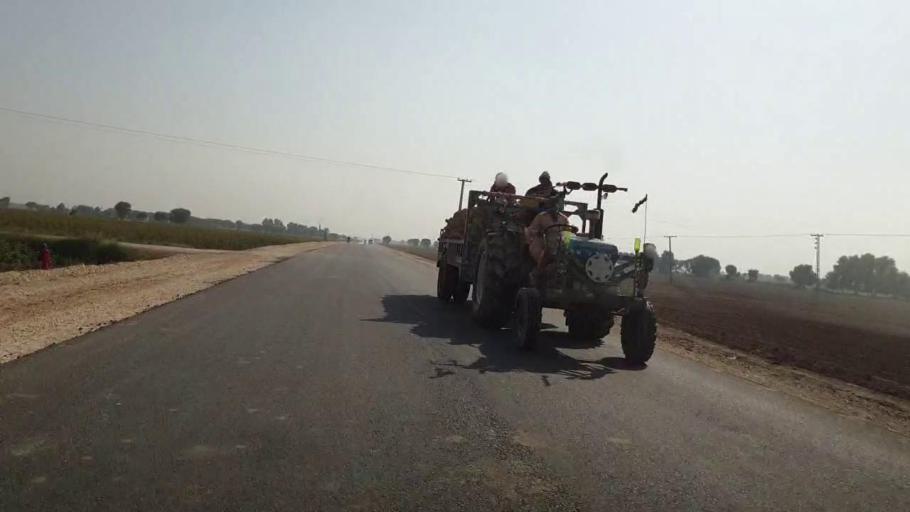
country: PK
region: Sindh
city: Dadu
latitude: 26.6678
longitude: 67.7765
